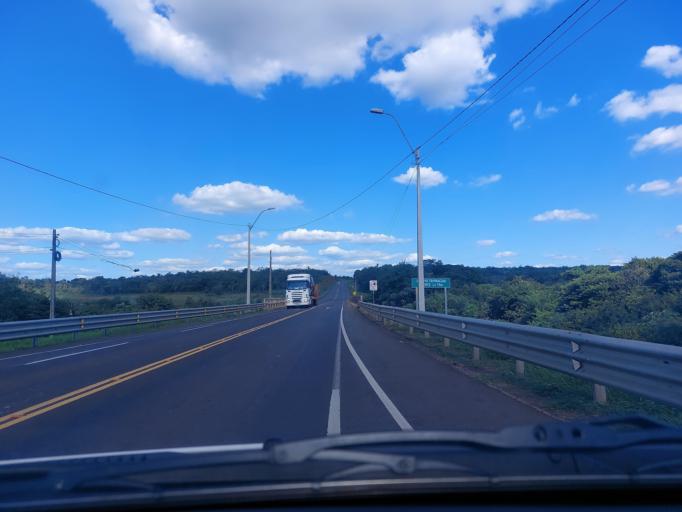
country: PY
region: San Pedro
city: Guayaybi
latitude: -24.6042
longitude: -56.4874
